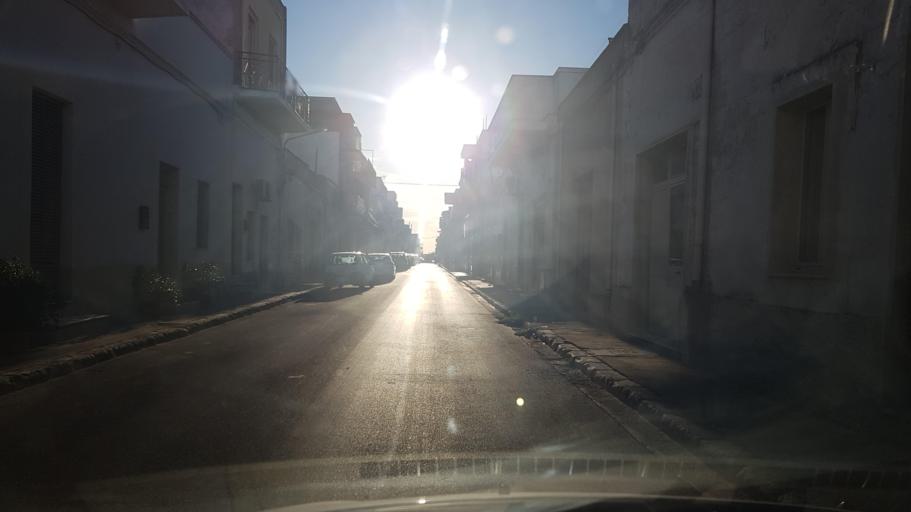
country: IT
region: Apulia
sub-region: Provincia di Brindisi
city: San Pancrazio Salentino
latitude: 40.4176
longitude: 17.8331
